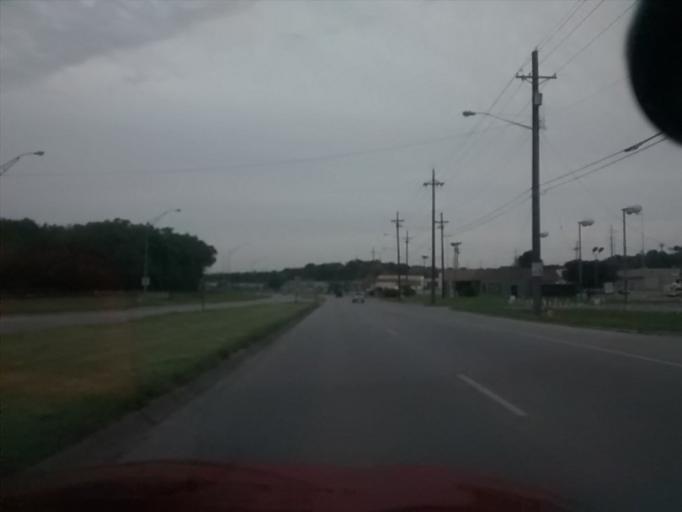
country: US
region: Nebraska
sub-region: Sarpy County
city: Bellevue
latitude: 41.1725
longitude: -95.9256
